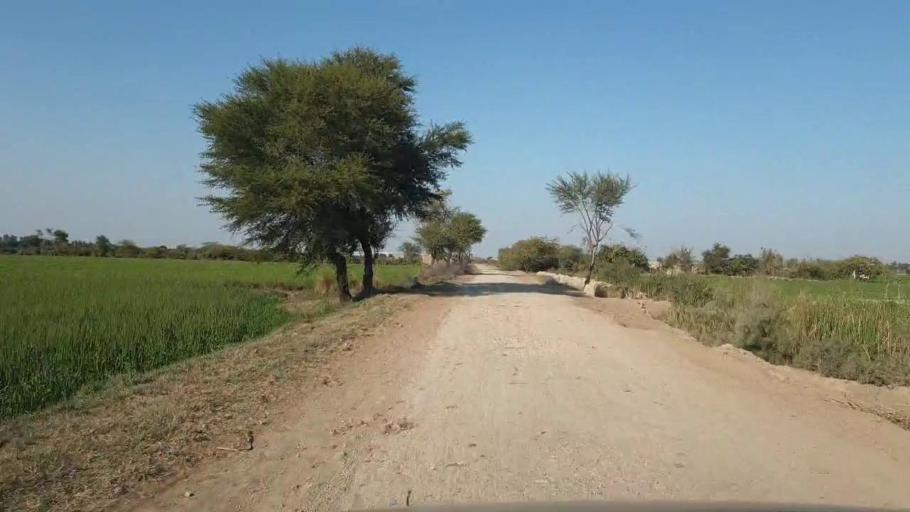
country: PK
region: Sindh
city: Shahpur Chakar
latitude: 26.1694
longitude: 68.6810
